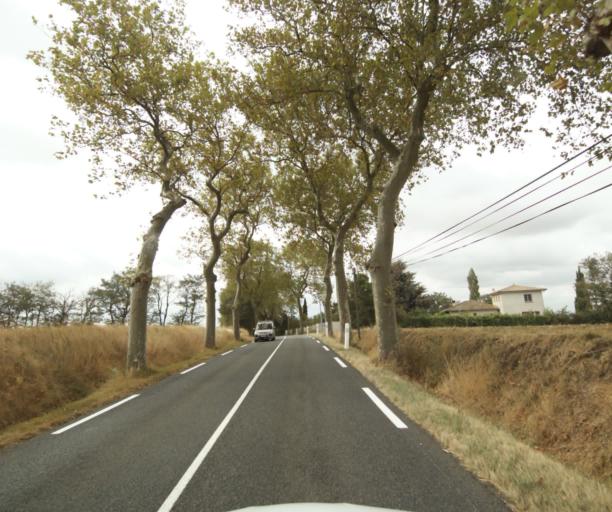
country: FR
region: Midi-Pyrenees
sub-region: Departement de la Haute-Garonne
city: Villefranche-de-Lauragais
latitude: 43.4202
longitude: 1.7187
